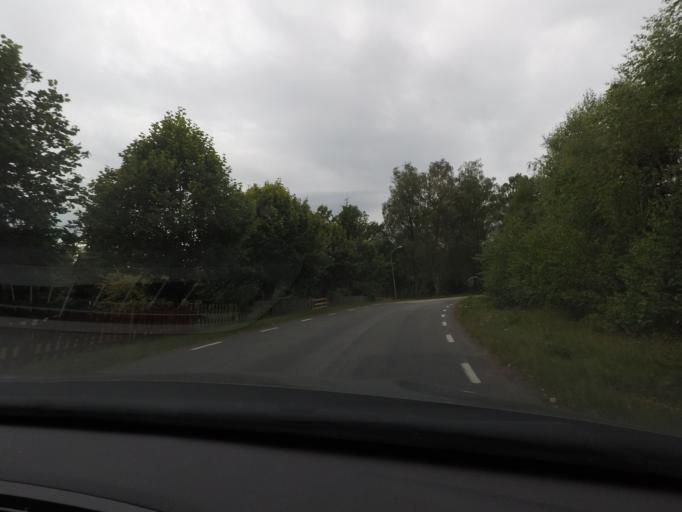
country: SE
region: Kronoberg
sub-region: Markaryds Kommun
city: Markaryd
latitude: 56.3958
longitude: 13.6563
